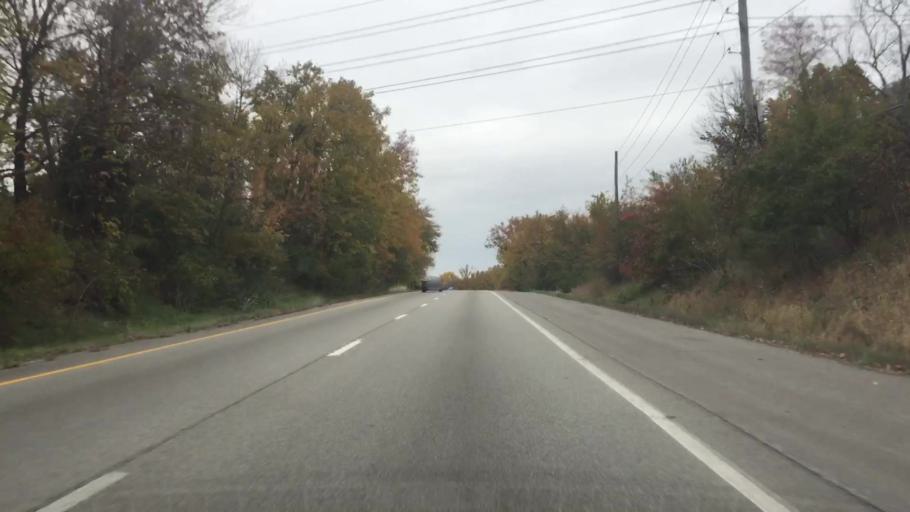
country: US
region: Missouri
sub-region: Jackson County
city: Raytown
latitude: 38.9709
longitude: -94.4378
